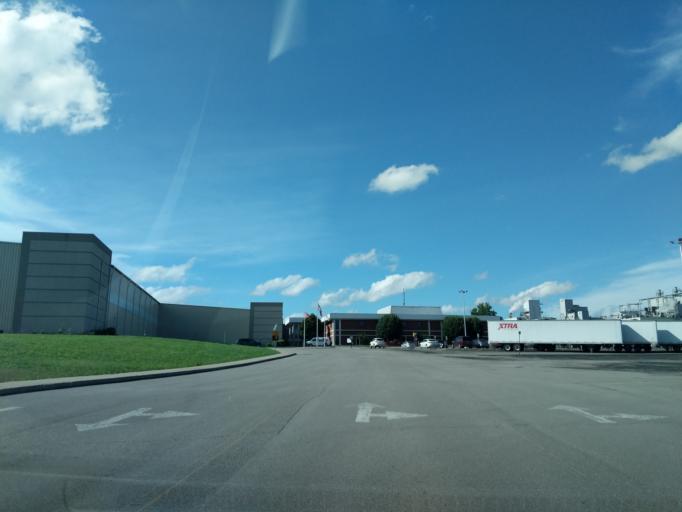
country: US
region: Tennessee
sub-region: Davidson County
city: Lakewood
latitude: 36.2670
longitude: -86.6561
